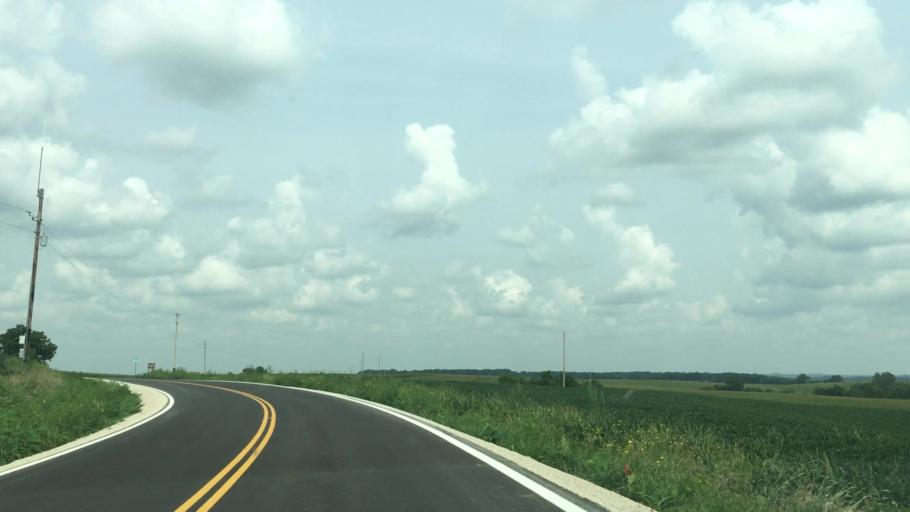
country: US
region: Minnesota
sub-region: Fillmore County
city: Preston
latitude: 43.7517
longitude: -92.0201
